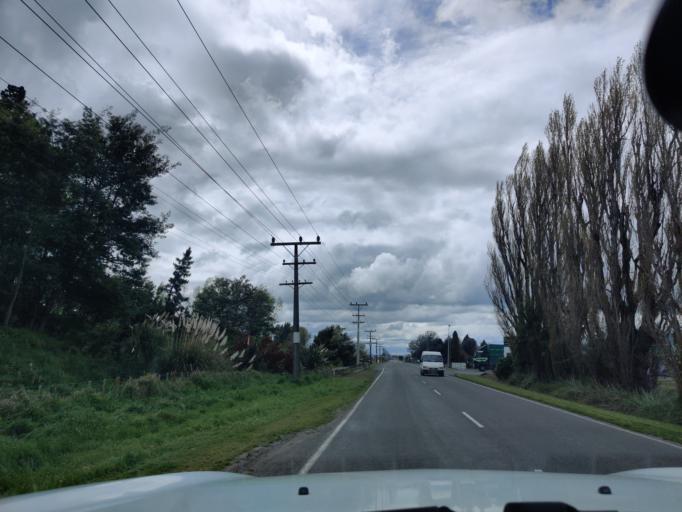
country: NZ
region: Manawatu-Wanganui
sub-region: Palmerston North City
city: Palmerston North
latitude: -40.2389
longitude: 175.5617
